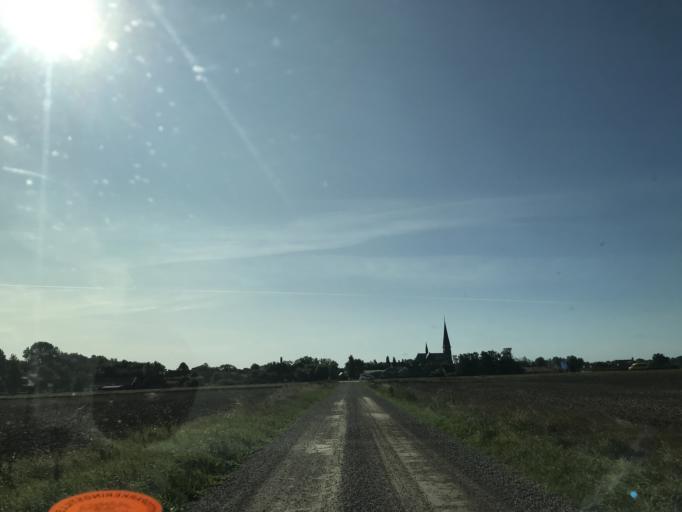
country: SE
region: Skane
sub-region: Landskrona
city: Asmundtorp
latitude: 55.8923
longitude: 12.9487
